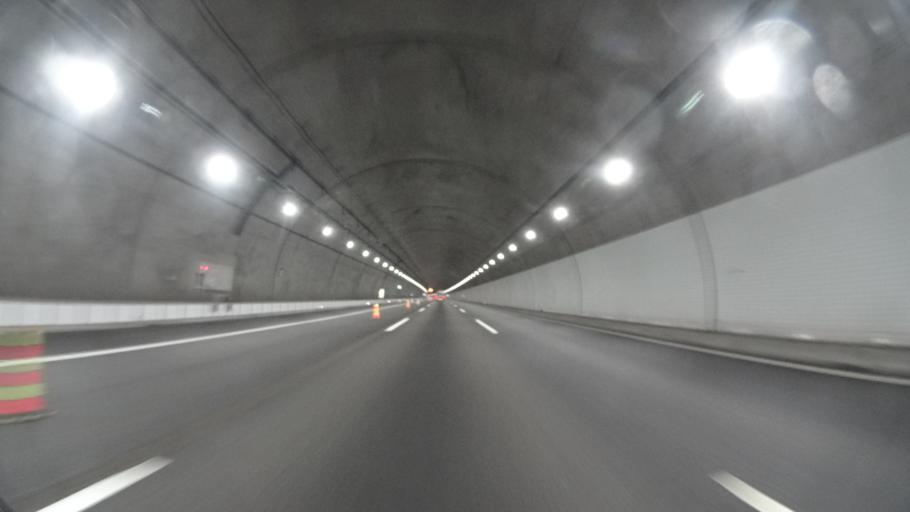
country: JP
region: Shizuoka
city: Shimada
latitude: 34.8807
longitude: 138.1955
